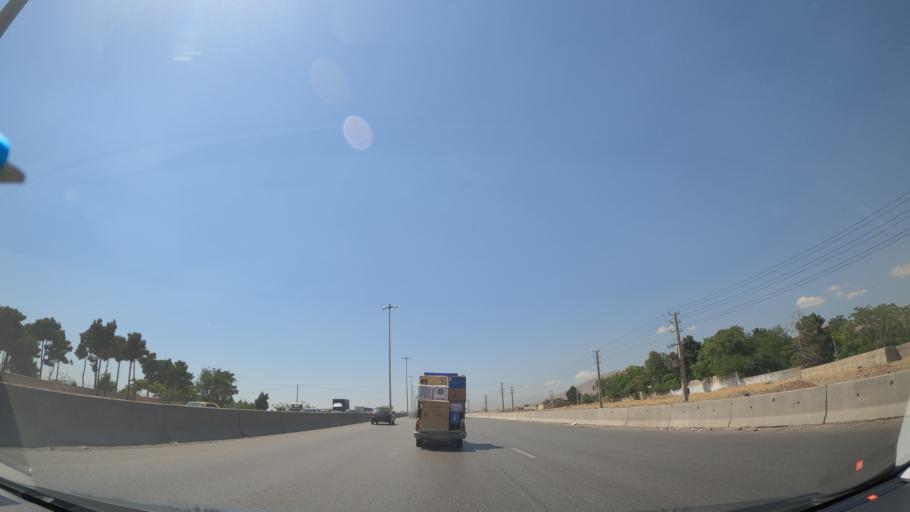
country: IR
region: Alborz
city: Karaj
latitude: 35.8723
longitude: 50.8959
